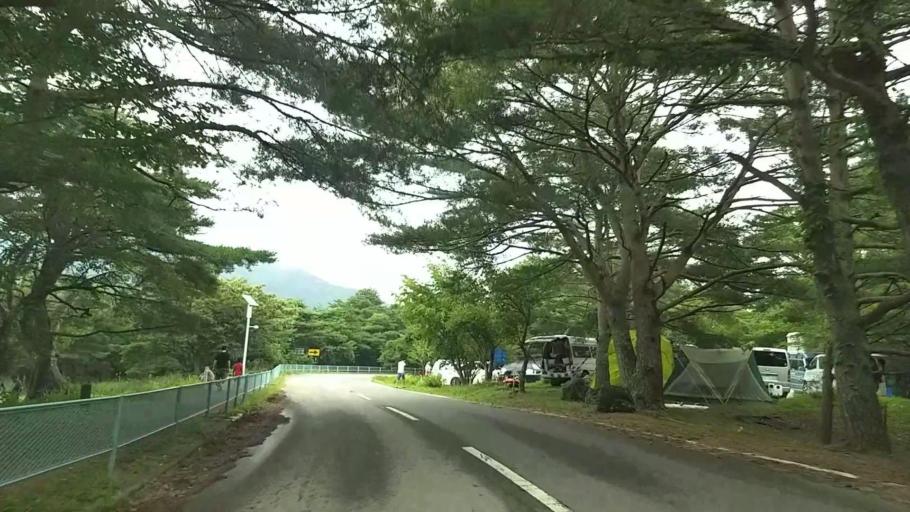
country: JP
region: Yamanashi
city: Fujikawaguchiko
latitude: 35.4589
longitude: 138.5997
